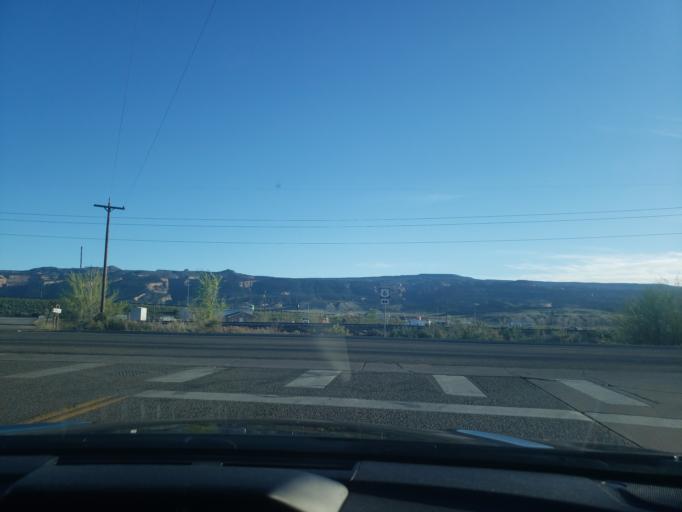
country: US
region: Colorado
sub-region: Mesa County
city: Fruita
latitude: 39.1584
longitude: -108.7384
